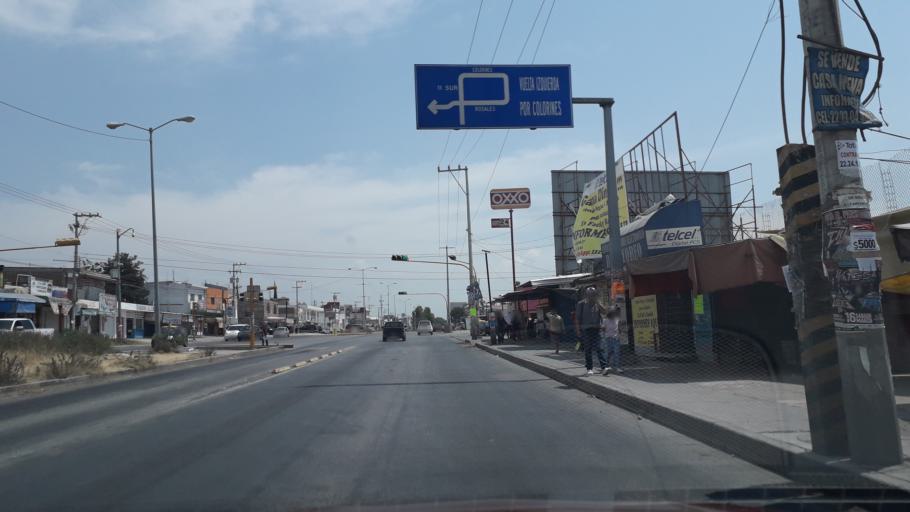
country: MX
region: Puebla
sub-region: Puebla
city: El Capulo (La Quebradora)
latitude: 18.9707
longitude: -98.2645
